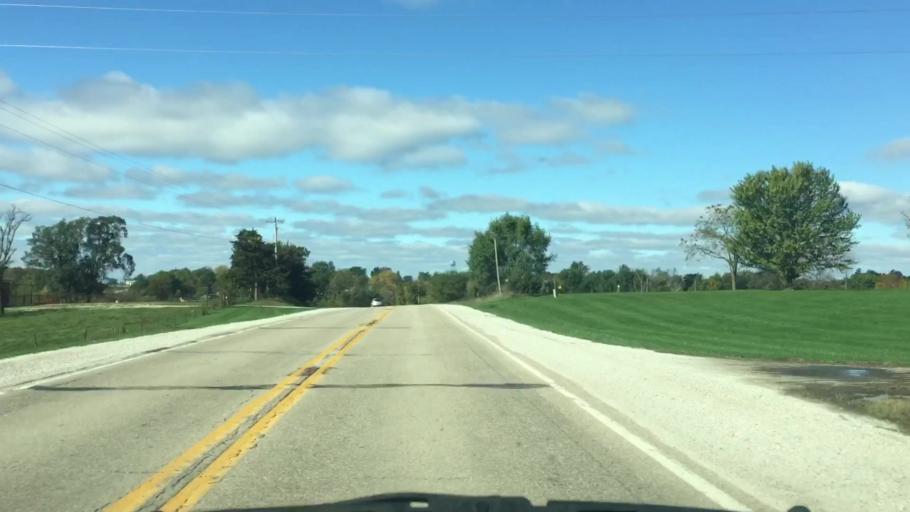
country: US
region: Iowa
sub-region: Decatur County
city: Leon
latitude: 40.7418
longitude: -93.8212
